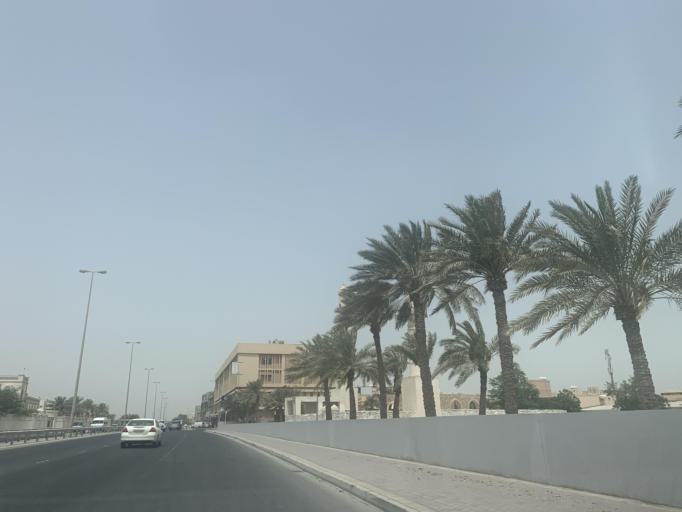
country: BH
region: Manama
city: Jidd Hafs
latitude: 26.2080
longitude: 50.5490
